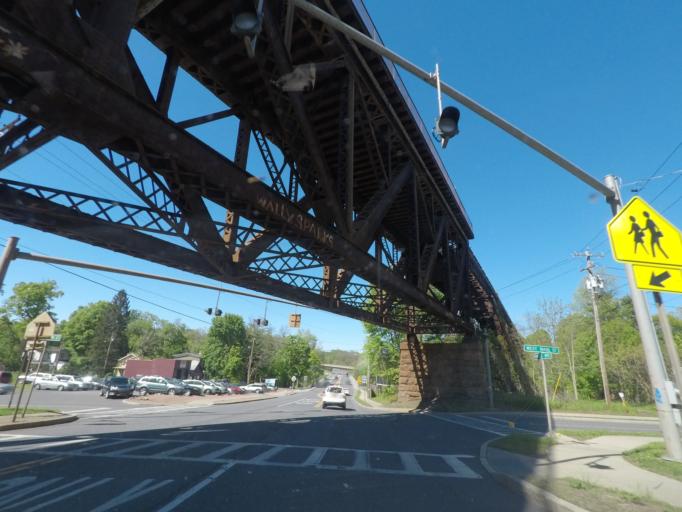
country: US
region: New York
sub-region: Greene County
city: Catskill
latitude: 42.2224
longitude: -73.8717
